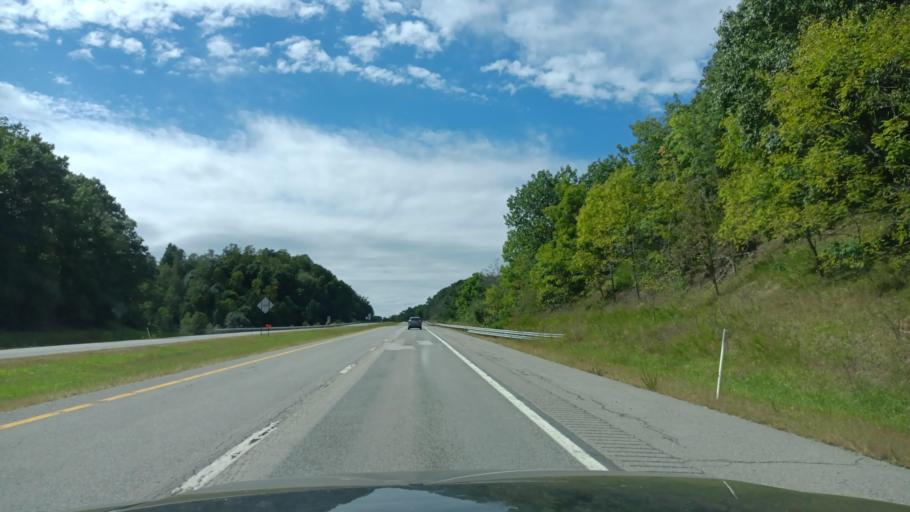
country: US
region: West Virginia
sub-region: Ritchie County
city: Harrisville
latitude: 39.2611
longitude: -81.1503
